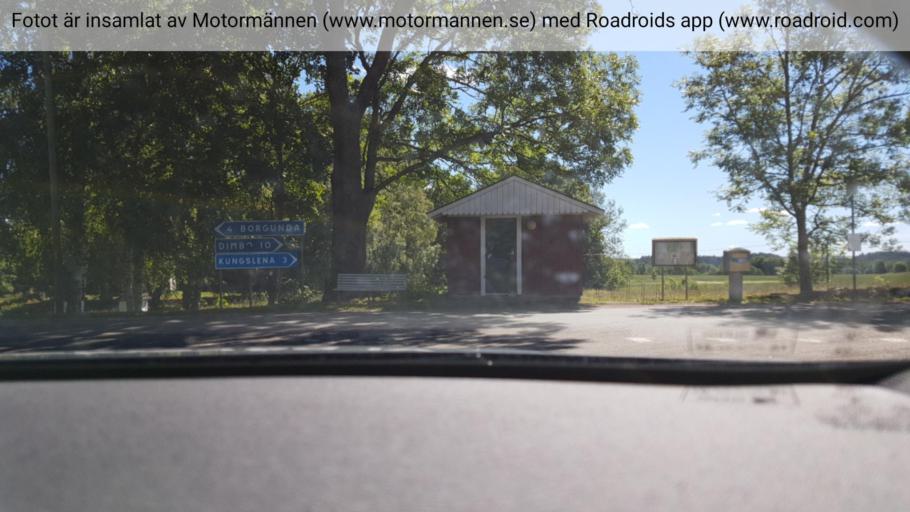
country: SE
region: Vaestra Goetaland
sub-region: Skovde Kommun
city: Skultorp
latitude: 58.2538
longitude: 13.7847
